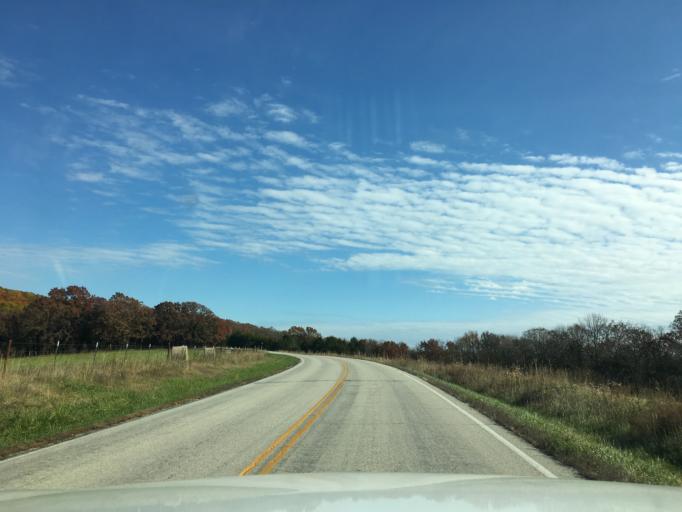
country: US
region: Missouri
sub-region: Maries County
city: Belle
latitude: 38.3355
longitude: -91.7787
